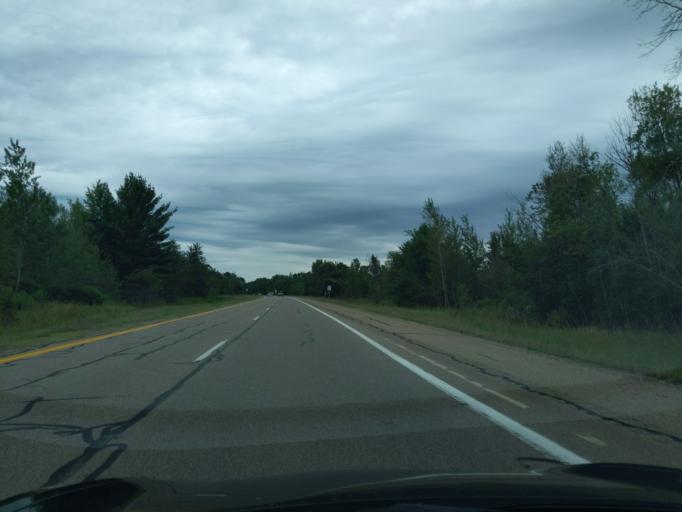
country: US
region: Michigan
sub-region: Roscommon County
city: Houghton Lake
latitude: 44.2643
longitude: -84.8040
